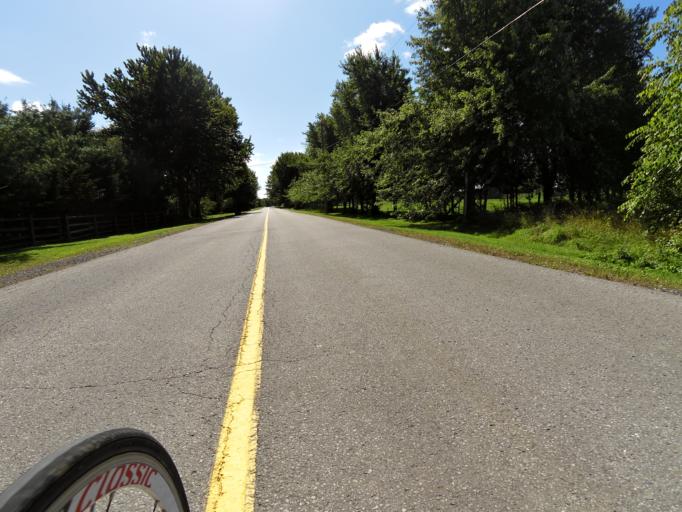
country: CA
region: Ontario
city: Bells Corners
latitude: 45.2413
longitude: -75.8088
